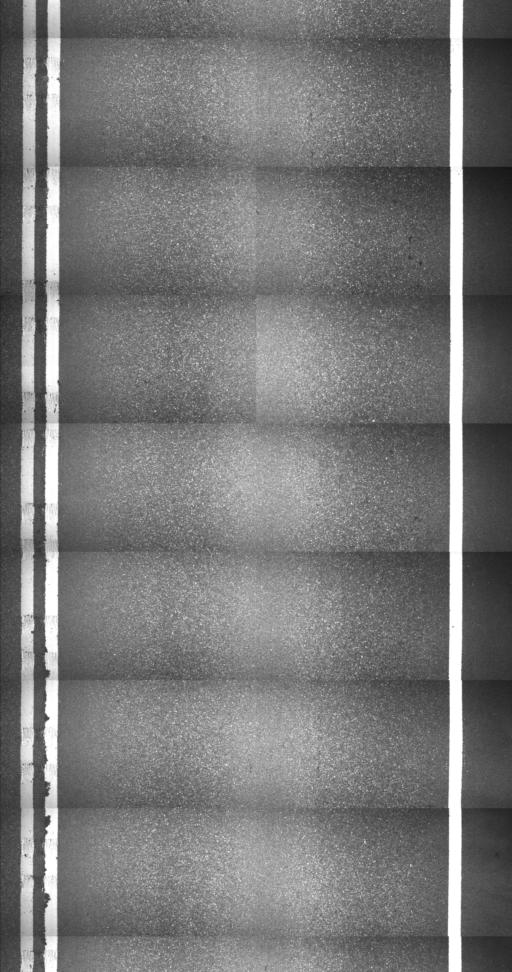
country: US
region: Vermont
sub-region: Washington County
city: Waterbury
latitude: 44.2612
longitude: -72.7878
